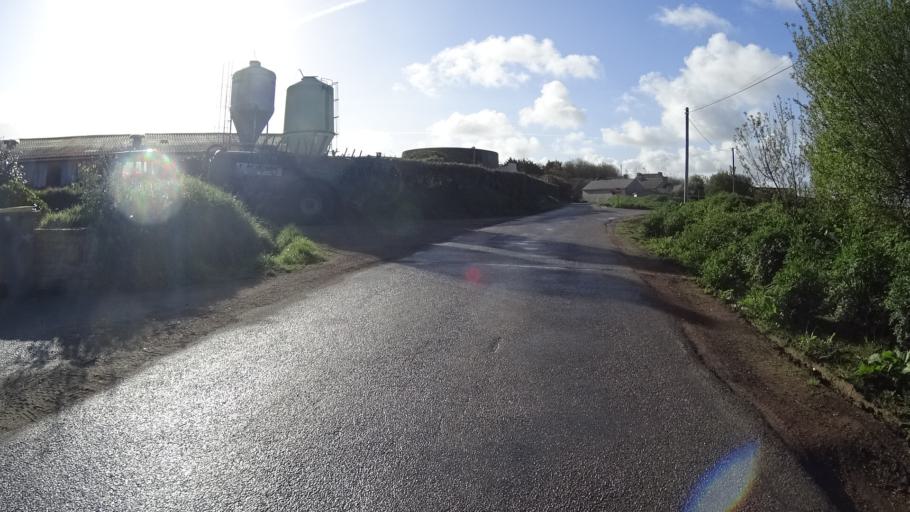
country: FR
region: Brittany
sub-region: Departement du Finistere
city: Plouarzel
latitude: 48.4280
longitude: -4.7049
